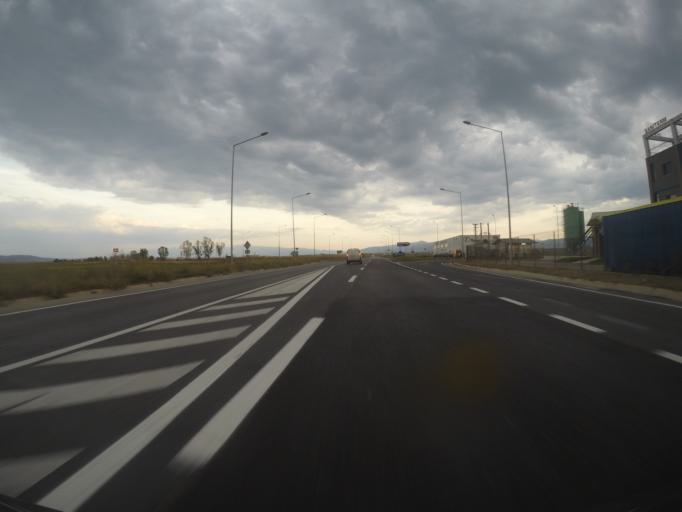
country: RO
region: Sibiu
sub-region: Comuna Sura Mica
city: Sura Mica
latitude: 45.8117
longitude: 24.0735
